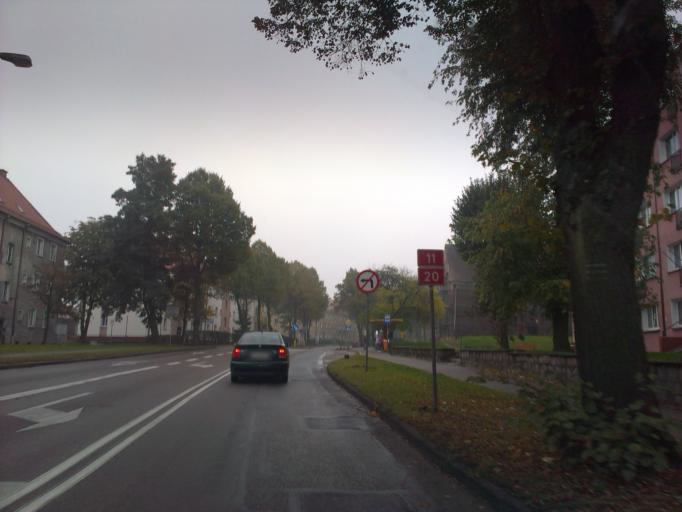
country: PL
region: West Pomeranian Voivodeship
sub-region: Powiat szczecinecki
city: Szczecinek
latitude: 53.7062
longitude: 16.7099
